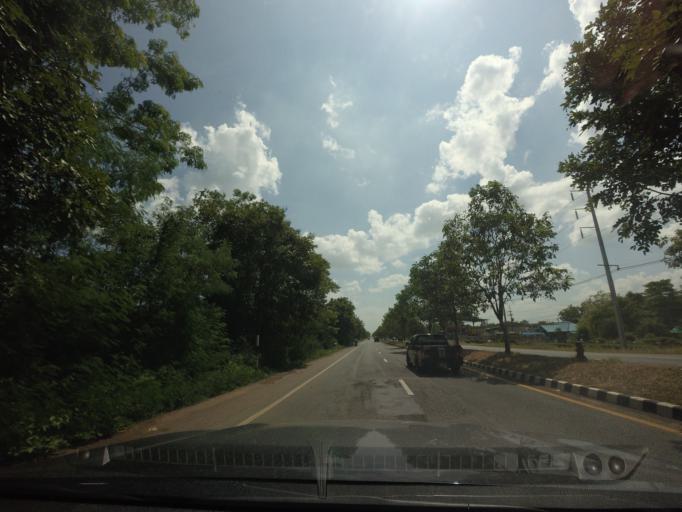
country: TH
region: Phetchabun
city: Nong Phai
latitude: 16.0271
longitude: 101.0753
